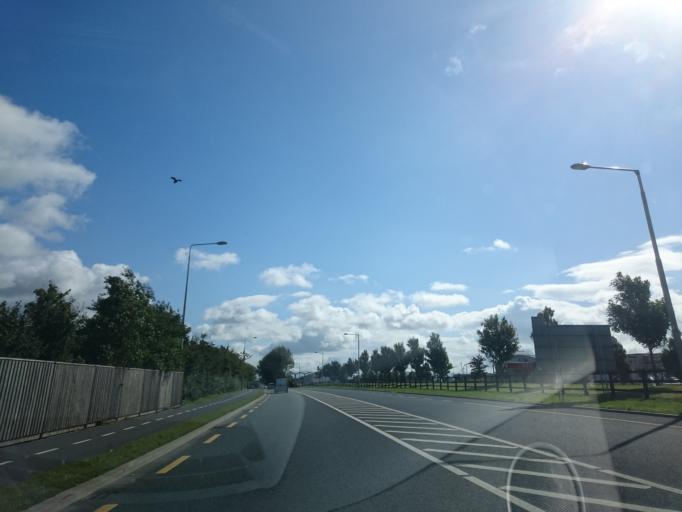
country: IE
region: Leinster
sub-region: Kilkenny
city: Kilkenny
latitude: 52.6356
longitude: -7.2472
